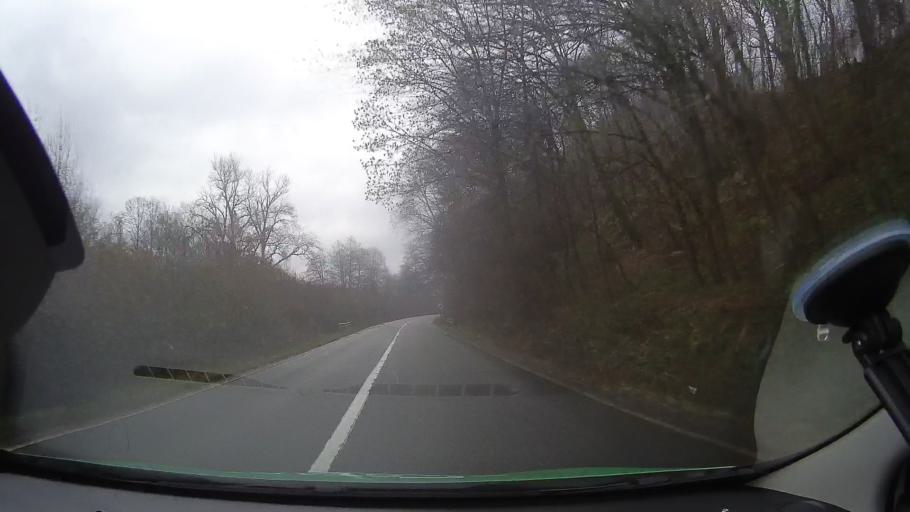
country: RO
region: Arad
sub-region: Comuna Almas
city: Almas
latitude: 46.3021
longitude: 22.1982
